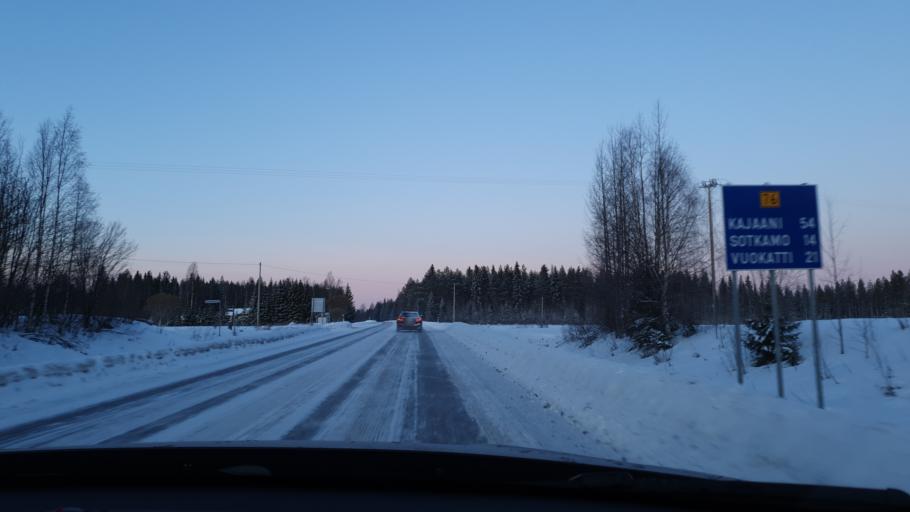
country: FI
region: Kainuu
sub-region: Kajaani
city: Sotkamo
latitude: 64.0755
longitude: 28.6505
